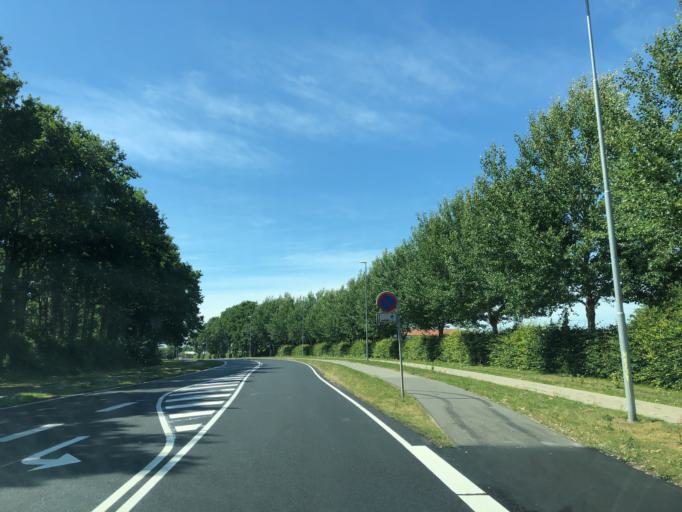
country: DK
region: Central Jutland
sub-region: Skive Kommune
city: Skive
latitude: 56.5543
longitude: 9.0185
